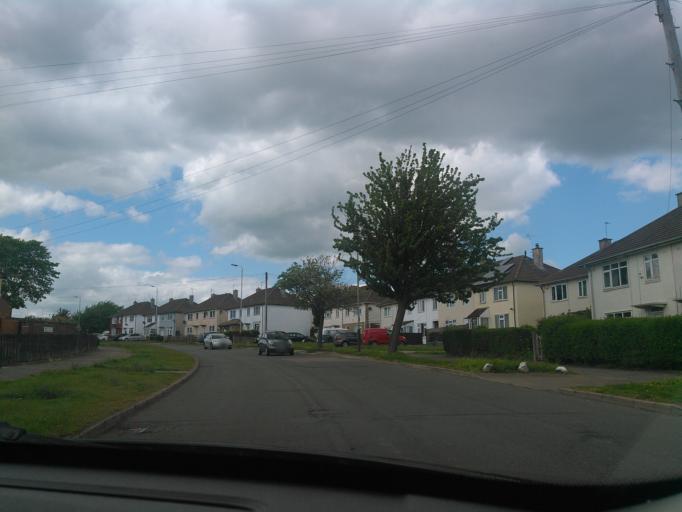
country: GB
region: England
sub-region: Leicestershire
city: Glenfield
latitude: 52.6344
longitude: -1.1911
